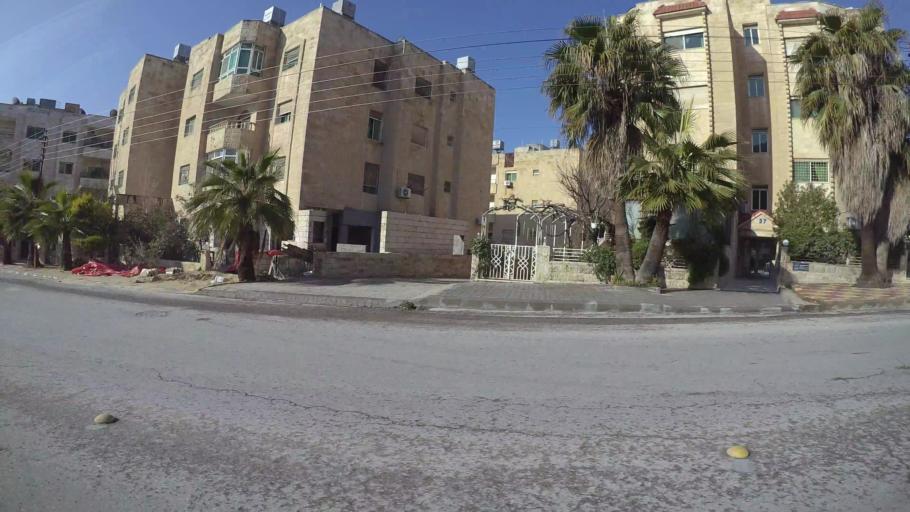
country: JO
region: Amman
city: Al Jubayhah
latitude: 32.0049
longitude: 35.8514
